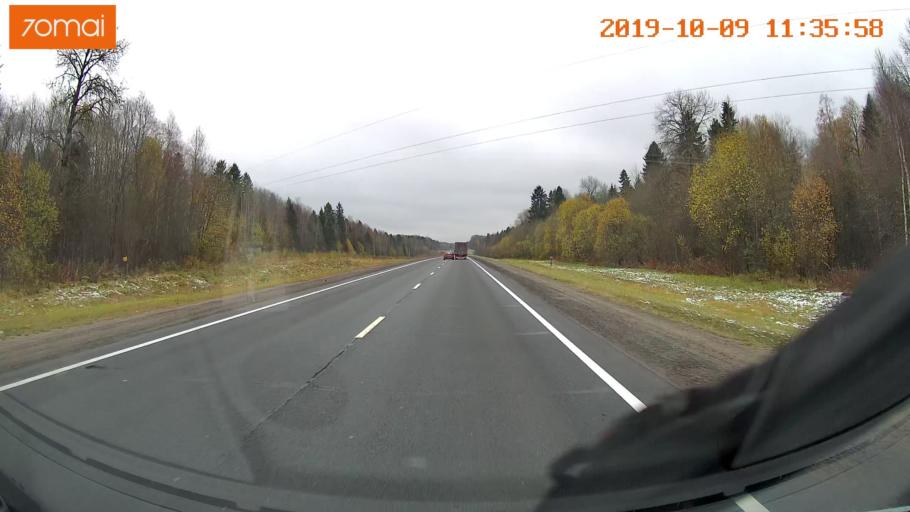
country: RU
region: Vologda
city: Gryazovets
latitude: 58.9968
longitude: 40.1316
